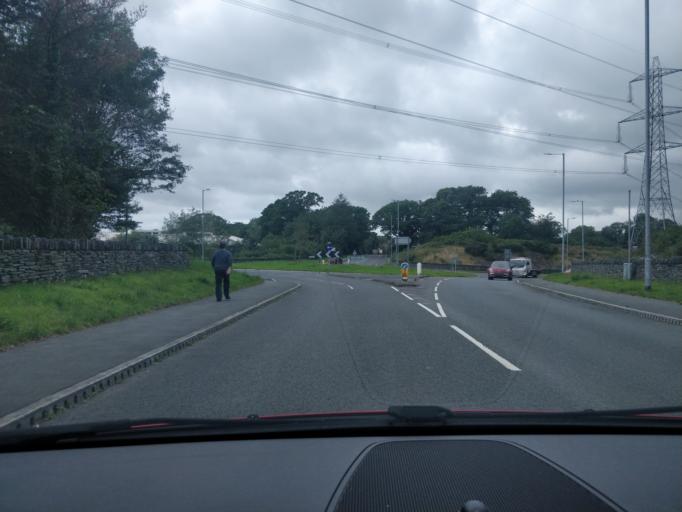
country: GB
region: Wales
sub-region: Gwynedd
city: Penrhyndeudraeth
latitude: 52.9267
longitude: -4.0801
